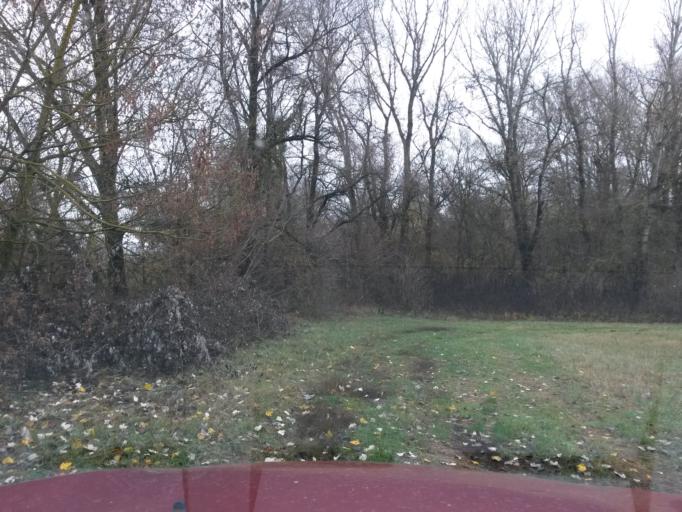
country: SK
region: Kosicky
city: Michalovce
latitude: 48.5609
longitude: 21.9502
